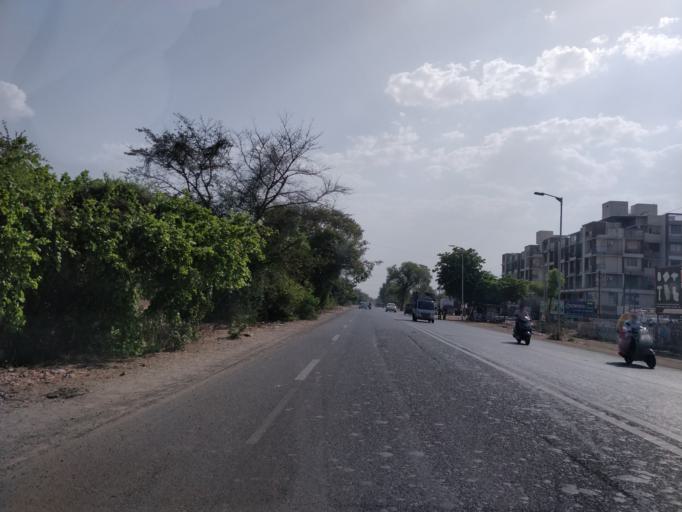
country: IN
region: Gujarat
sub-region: Ahmadabad
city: Naroda
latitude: 23.0823
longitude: 72.6742
